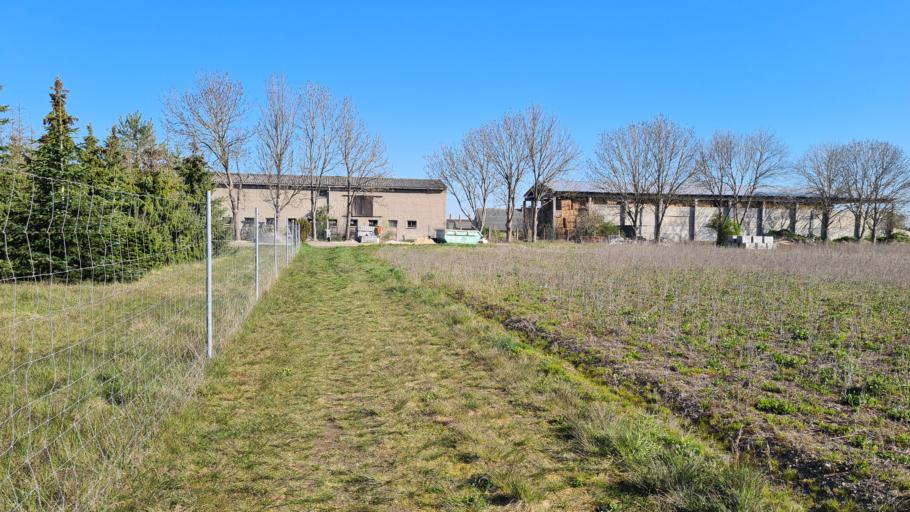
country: DE
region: Brandenburg
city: Ruckersdorf
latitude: 51.5547
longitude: 13.5974
